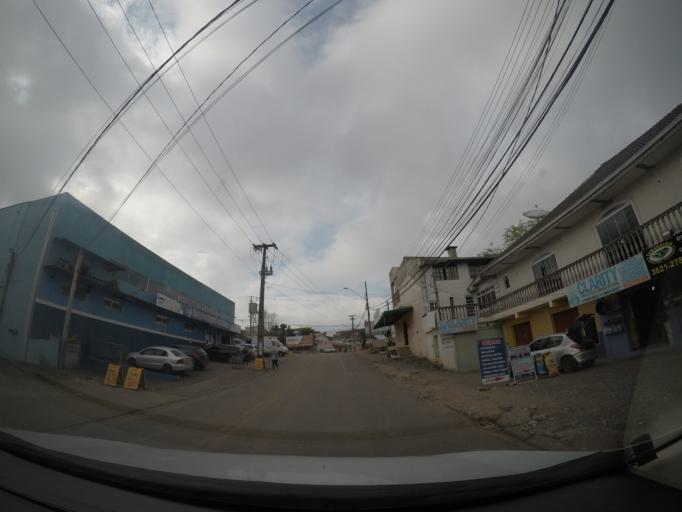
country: BR
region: Parana
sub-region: Colombo
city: Colombo
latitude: -25.3511
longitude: -49.2128
